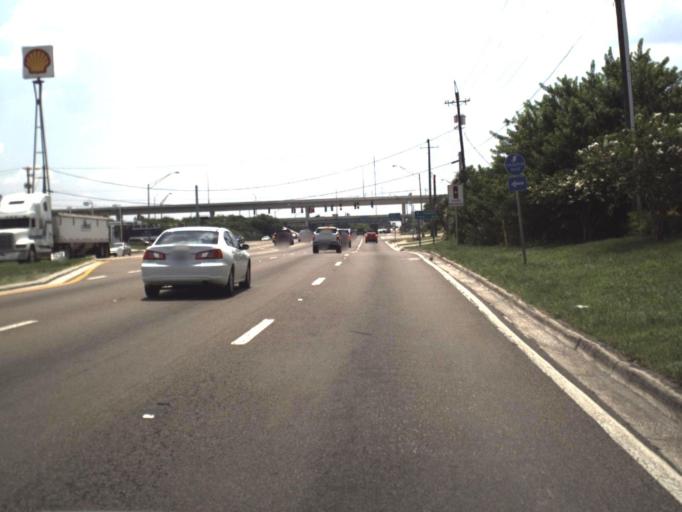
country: US
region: Florida
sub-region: Hillsborough County
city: East Lake-Orient Park
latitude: 27.9539
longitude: -82.4019
